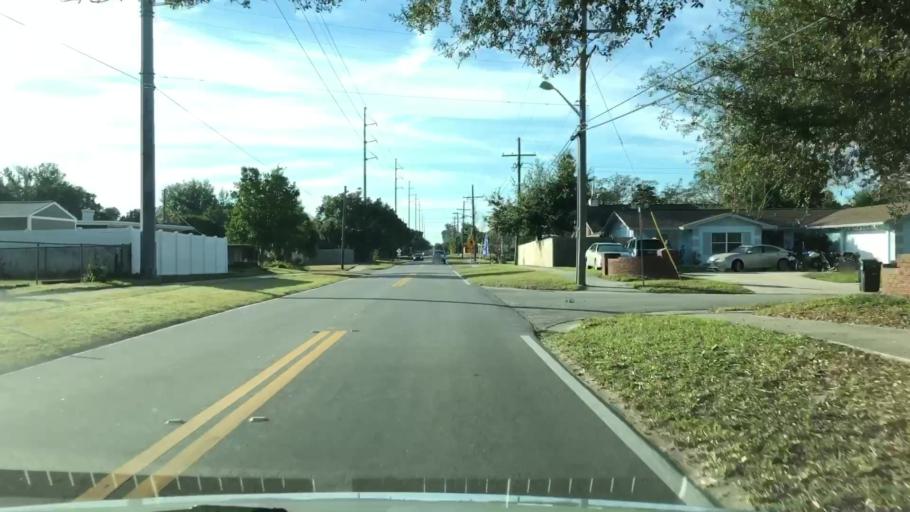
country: US
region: Florida
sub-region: Orange County
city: Conway
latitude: 28.5212
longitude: -81.3393
